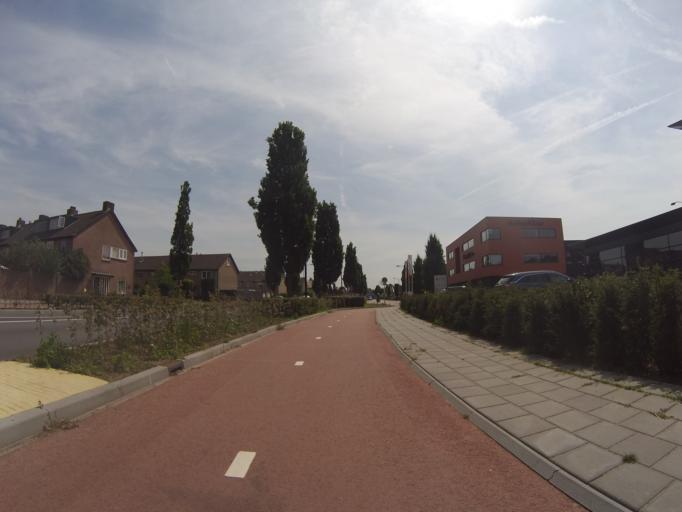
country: NL
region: Gelderland
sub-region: Gemeente Putten
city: Putten
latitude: 52.2512
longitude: 5.5994
